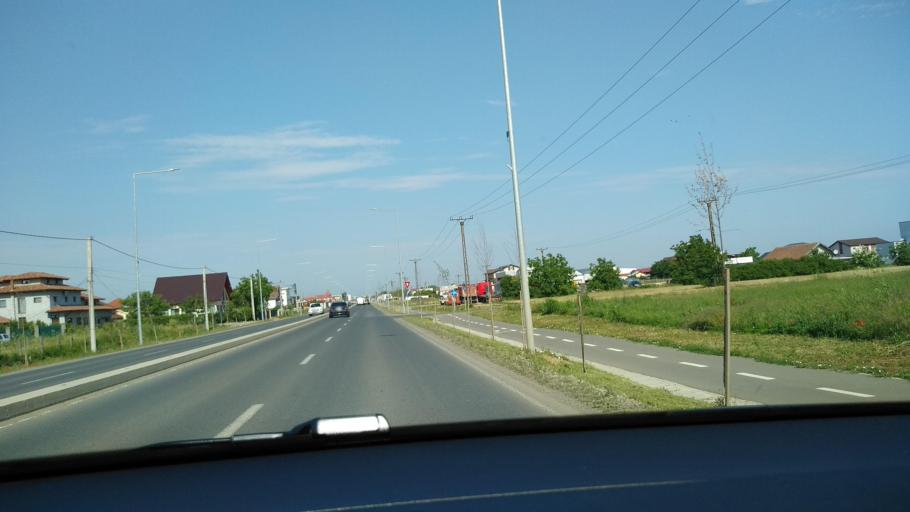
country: RO
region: Timis
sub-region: Comuna Mosnita Noua
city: Mosnita Noua
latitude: 45.7216
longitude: 21.3082
